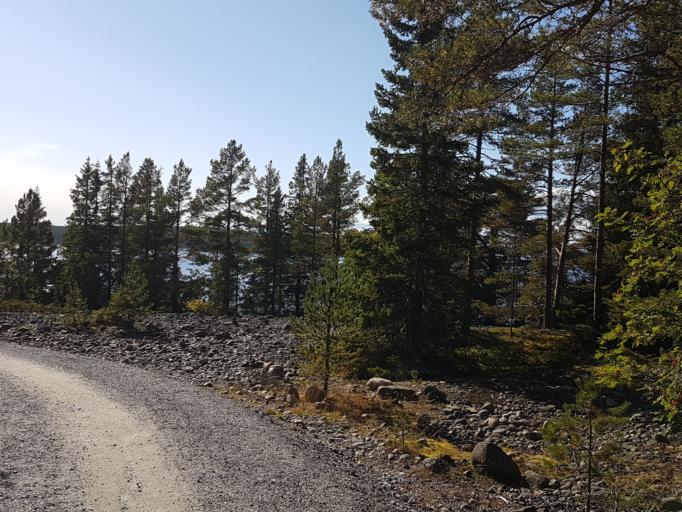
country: SE
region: Vaesterbotten
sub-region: Skelleftea Kommun
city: Skelleftehamn
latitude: 64.4795
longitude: 21.5730
